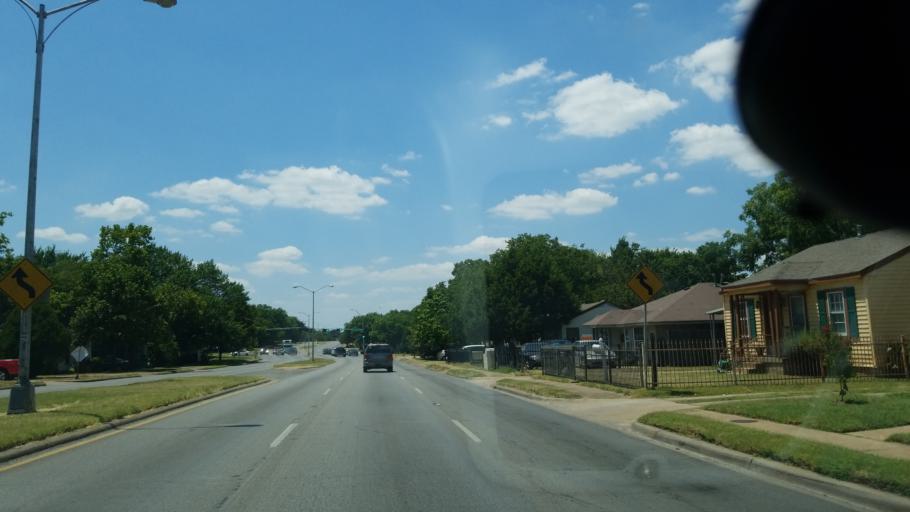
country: US
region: Texas
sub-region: Dallas County
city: Cockrell Hill
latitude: 32.7205
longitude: -96.8468
